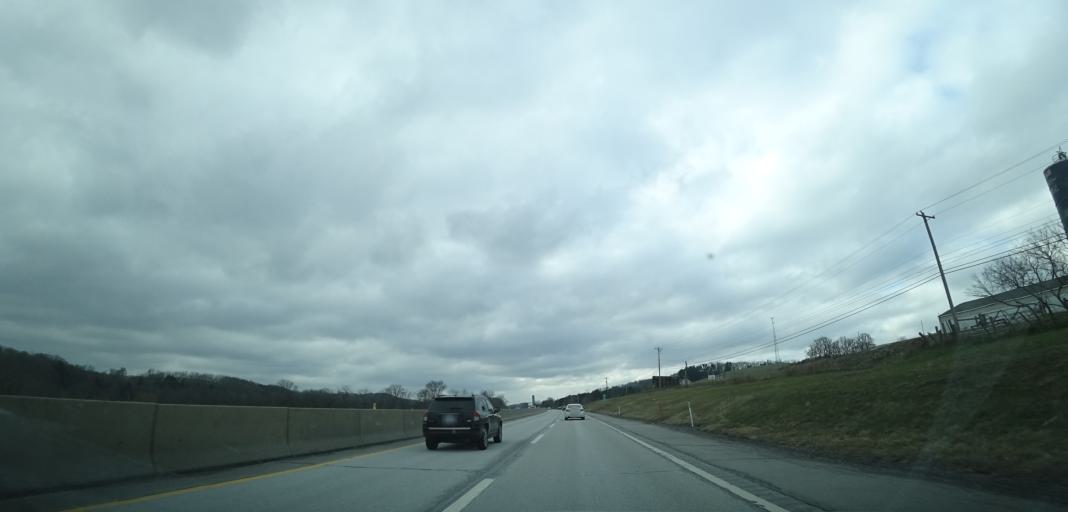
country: US
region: Pennsylvania
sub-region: Butler County
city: Fernway
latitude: 40.7356
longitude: -80.1714
